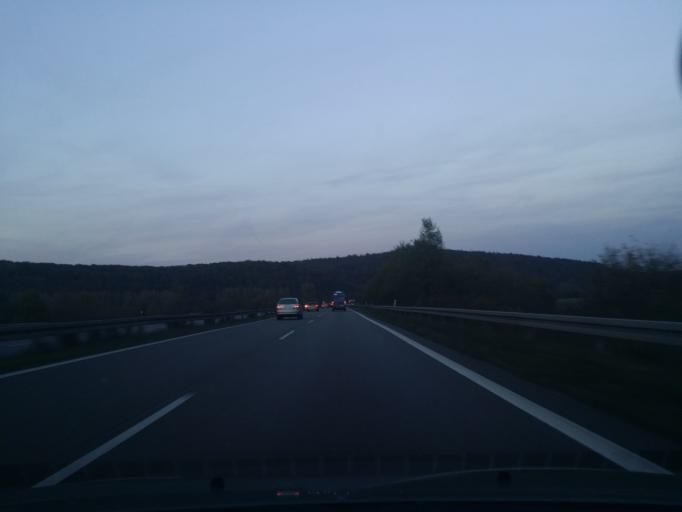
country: DE
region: Baden-Wuerttemberg
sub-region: Tuebingen Region
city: Kusterdingen
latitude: 48.5329
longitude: 9.1125
